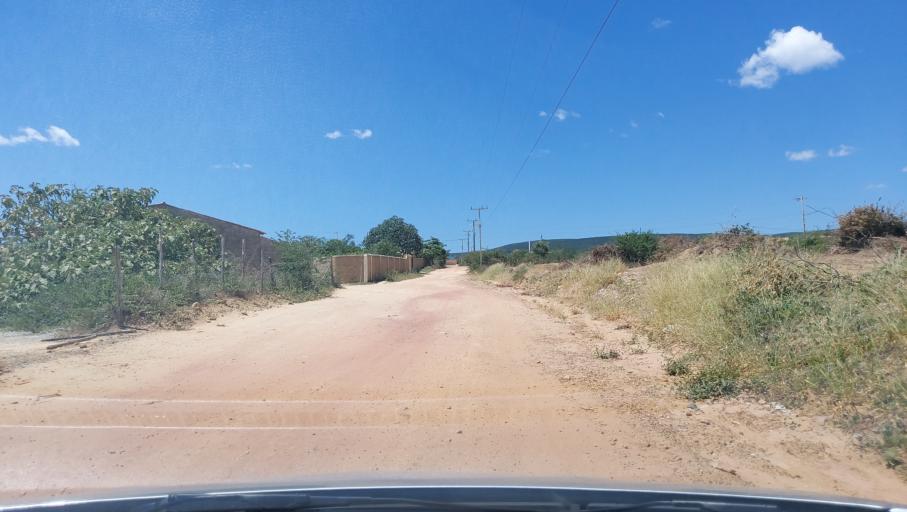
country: BR
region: Bahia
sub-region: Oliveira Dos Brejinhos
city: Beira Rio
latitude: -12.0038
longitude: -42.6318
